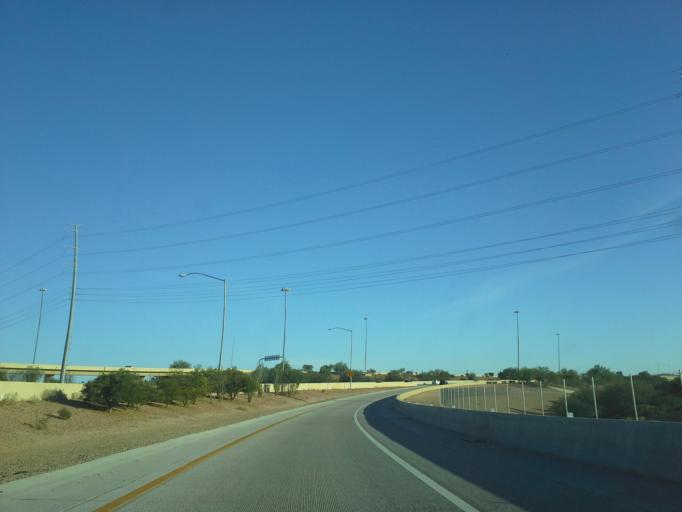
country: US
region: Arizona
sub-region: Maricopa County
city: Paradise Valley
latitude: 33.6707
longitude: -112.0024
